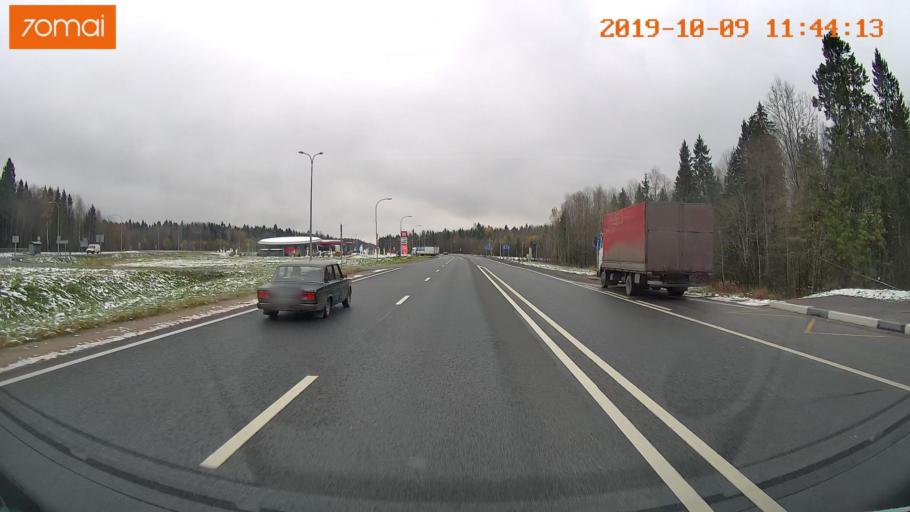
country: RU
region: Vologda
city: Gryazovets
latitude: 58.8861
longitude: 40.1900
